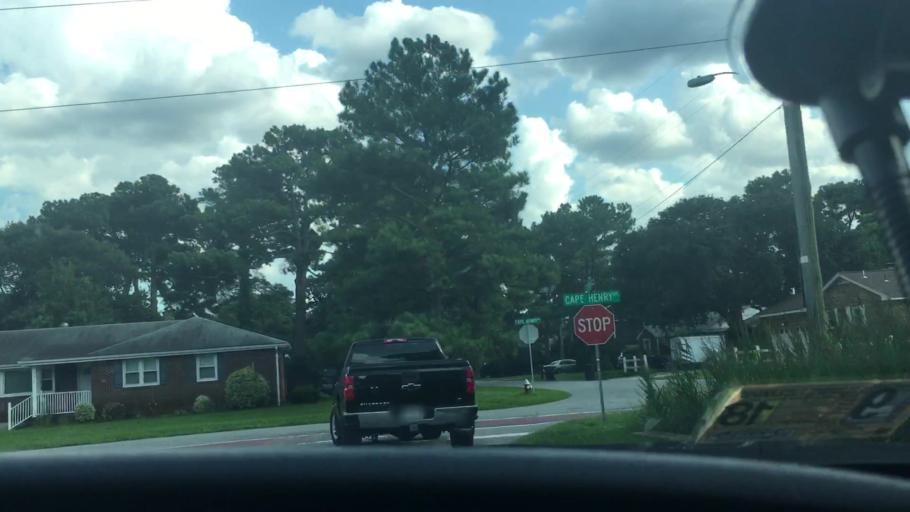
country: US
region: Virginia
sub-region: City of Virginia Beach
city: Virginia Beach
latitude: 36.9091
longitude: -76.0774
